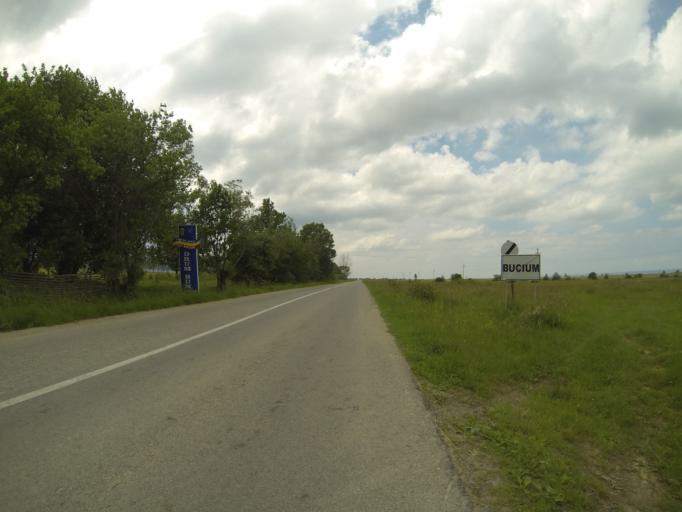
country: RO
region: Brasov
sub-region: Comuna Harseni
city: Harseni
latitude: 45.7397
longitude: 25.0904
